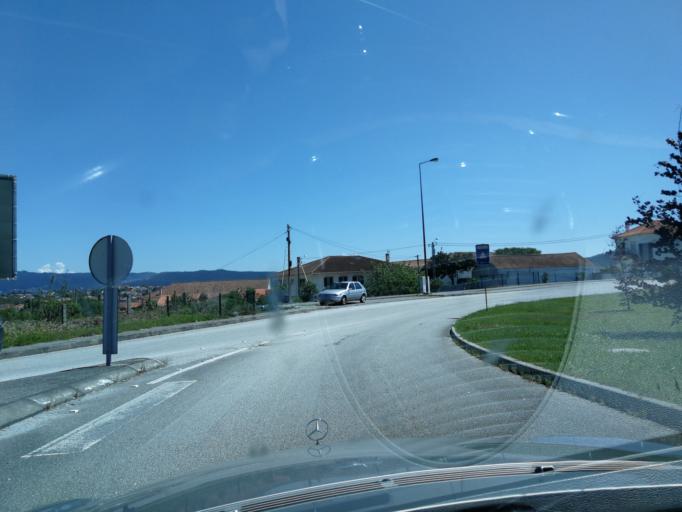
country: PT
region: Viana do Castelo
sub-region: Viana do Castelo
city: Meadela
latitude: 41.7100
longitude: -8.8027
